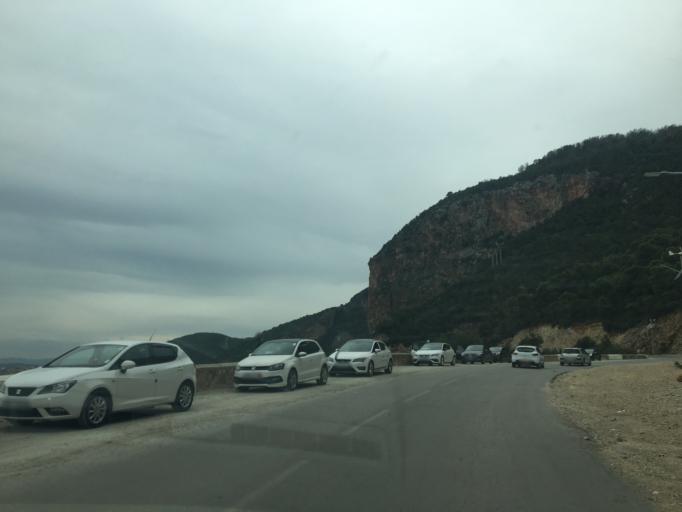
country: DZ
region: Tipaza
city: Tipasa
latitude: 36.6177
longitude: 2.4058
